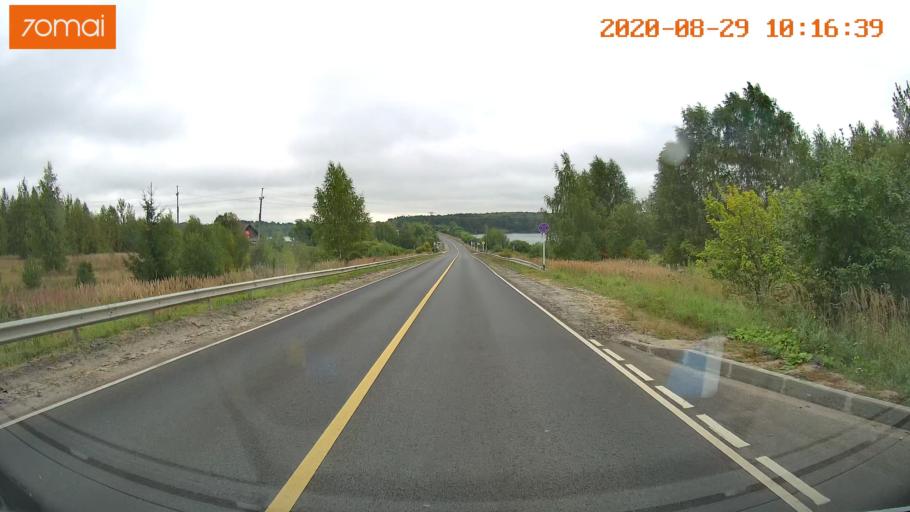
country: RU
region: Ivanovo
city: Yur'yevets
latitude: 57.3374
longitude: 42.7954
